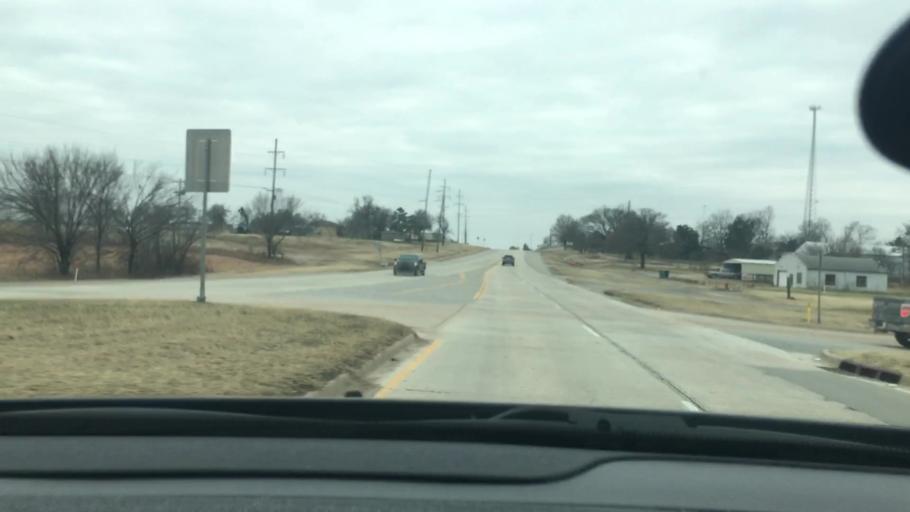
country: US
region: Oklahoma
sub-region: Carter County
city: Healdton
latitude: 34.4475
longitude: -97.5097
